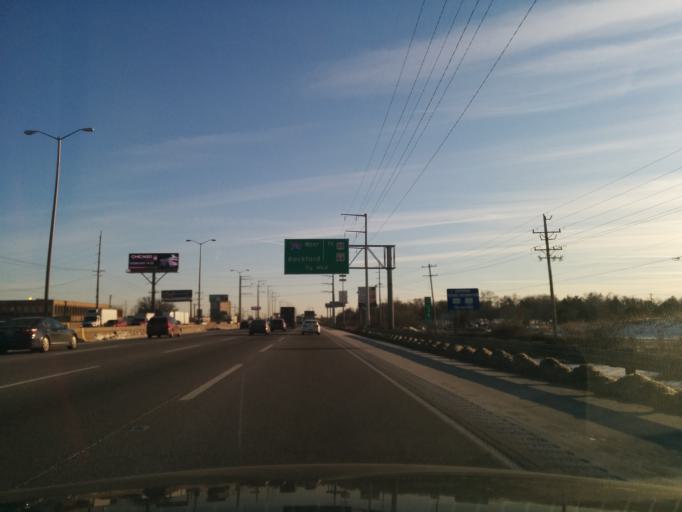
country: US
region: Illinois
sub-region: Cook County
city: Northlake
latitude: 41.9158
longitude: -87.9200
